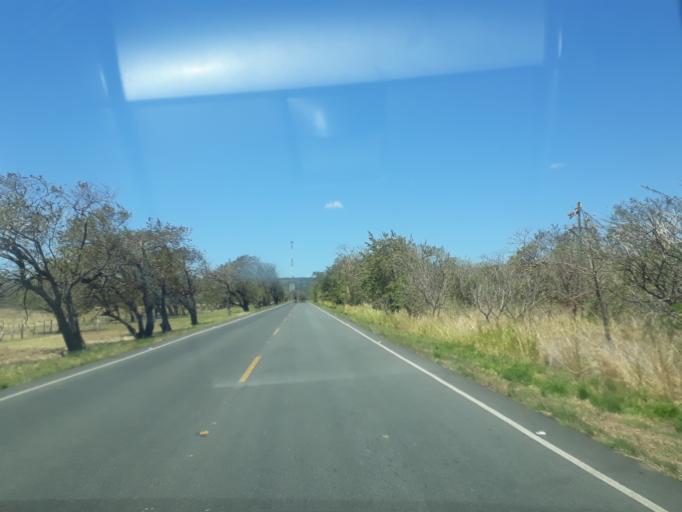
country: CR
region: Guanacaste
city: Liberia
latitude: 10.8246
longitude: -85.5501
